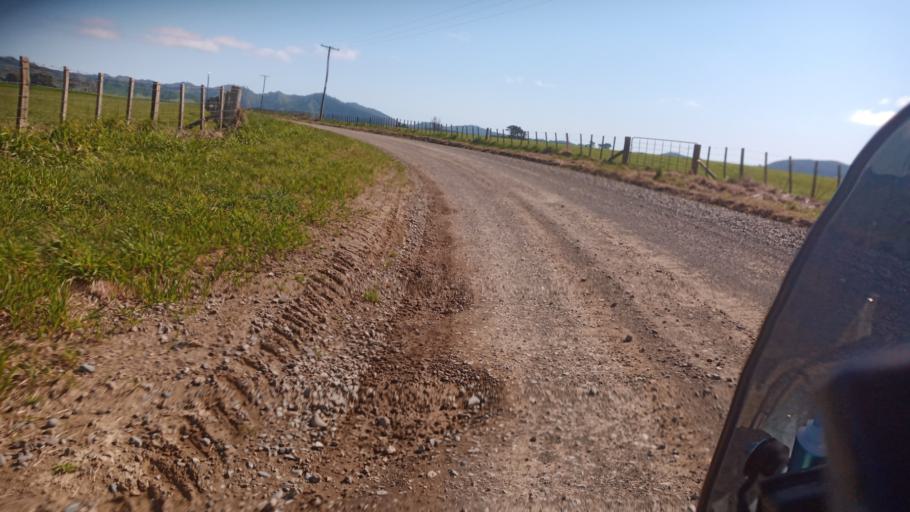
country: NZ
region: Gisborne
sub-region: Gisborne District
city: Gisborne
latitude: -39.1306
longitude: 177.9454
